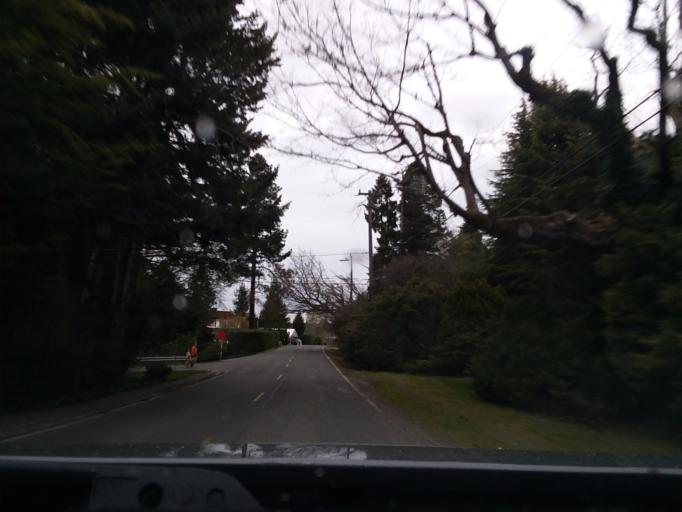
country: US
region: Washington
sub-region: King County
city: Shoreline
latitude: 47.6988
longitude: -122.3934
